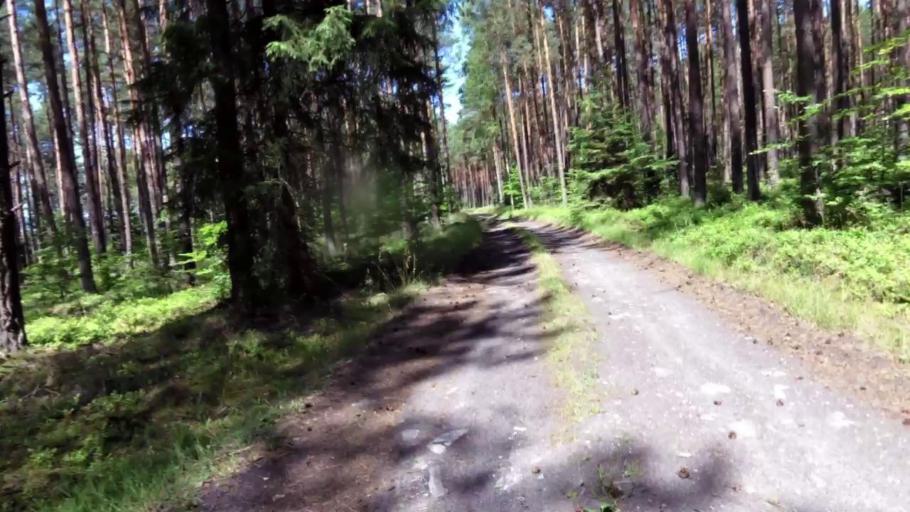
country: PL
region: West Pomeranian Voivodeship
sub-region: Powiat bialogardzki
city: Bialogard
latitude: 53.9503
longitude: 16.1128
